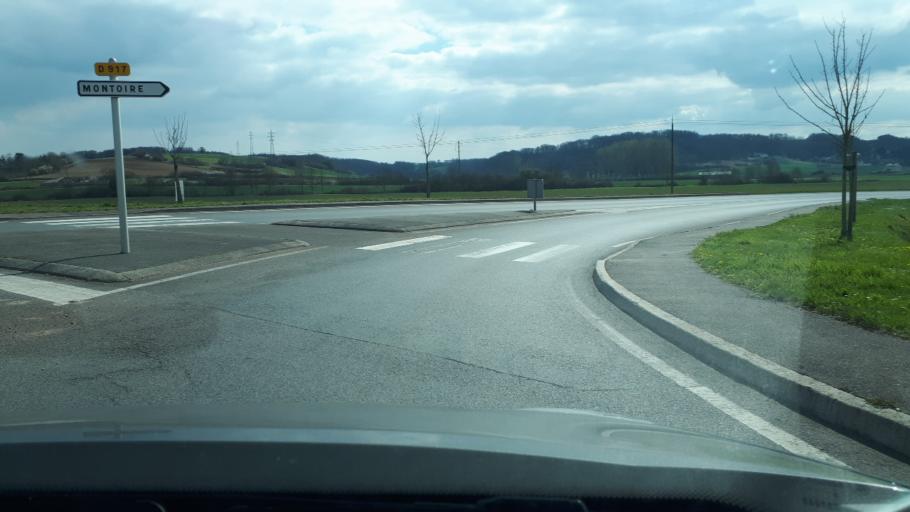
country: FR
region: Centre
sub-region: Departement du Loir-et-Cher
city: Lunay
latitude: 47.7702
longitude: 0.9108
